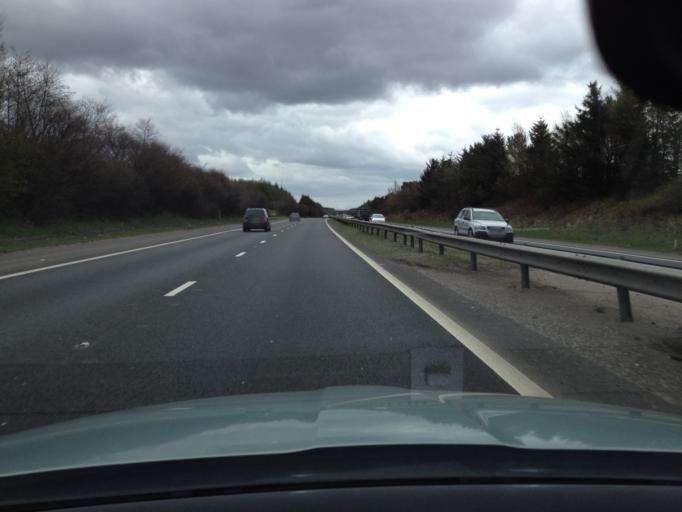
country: GB
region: Scotland
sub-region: North Lanarkshire
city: Caldercruix
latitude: 55.8448
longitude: -3.8873
